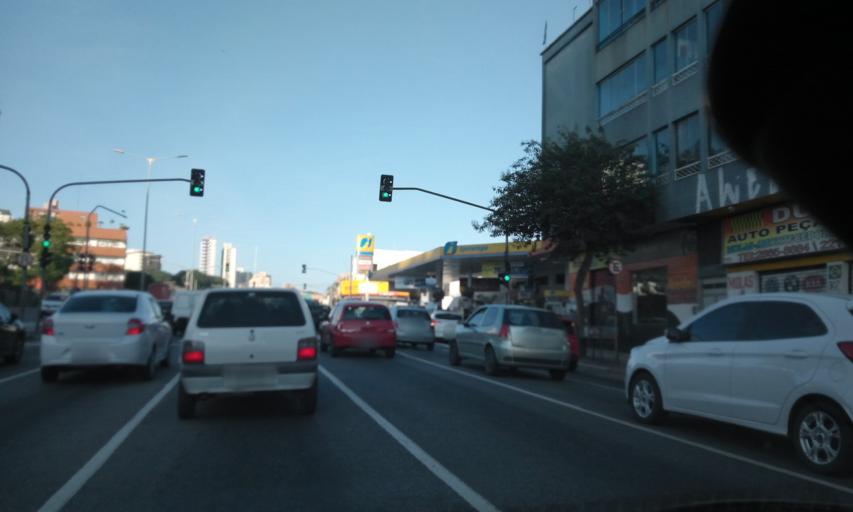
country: BR
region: Sao Paulo
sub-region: Santo Andre
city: Santo Andre
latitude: -23.6655
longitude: -46.5185
